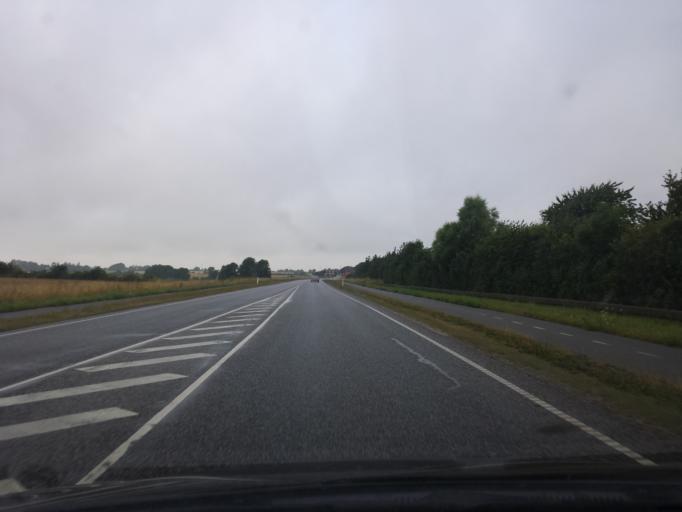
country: DK
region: South Denmark
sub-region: Sonderborg Kommune
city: Guderup
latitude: 54.9963
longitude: 9.8546
